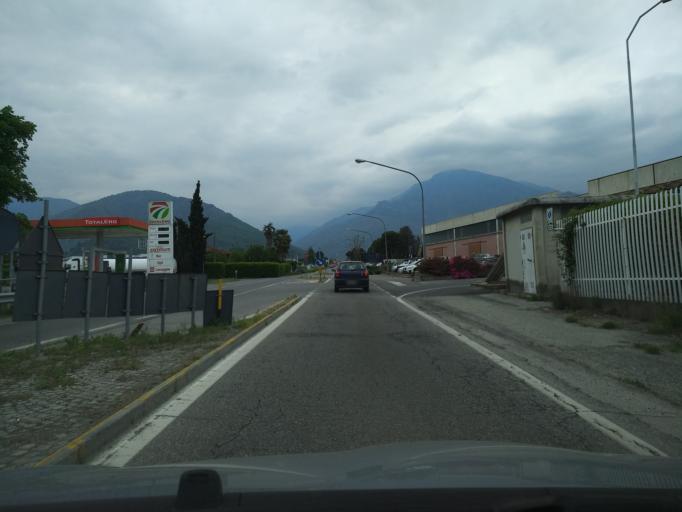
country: IT
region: Piedmont
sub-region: Provincia di Torino
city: Airali
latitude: 44.8117
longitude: 7.2669
